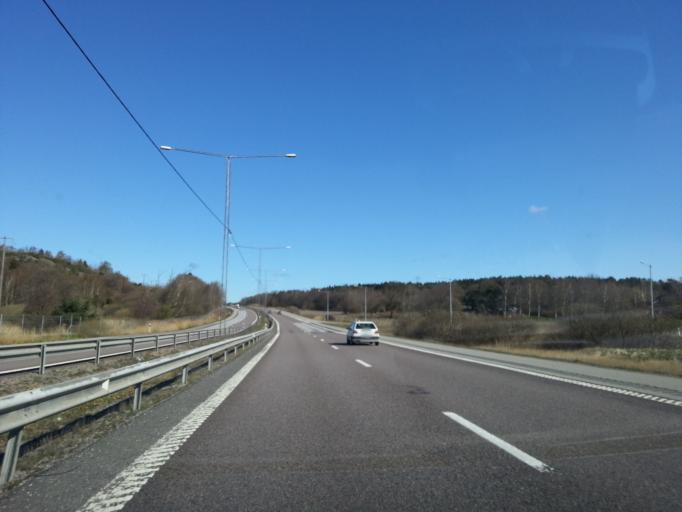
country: SE
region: Vaestra Goetaland
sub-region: Stenungsunds Kommun
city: Stora Hoga
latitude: 58.0273
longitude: 11.8465
